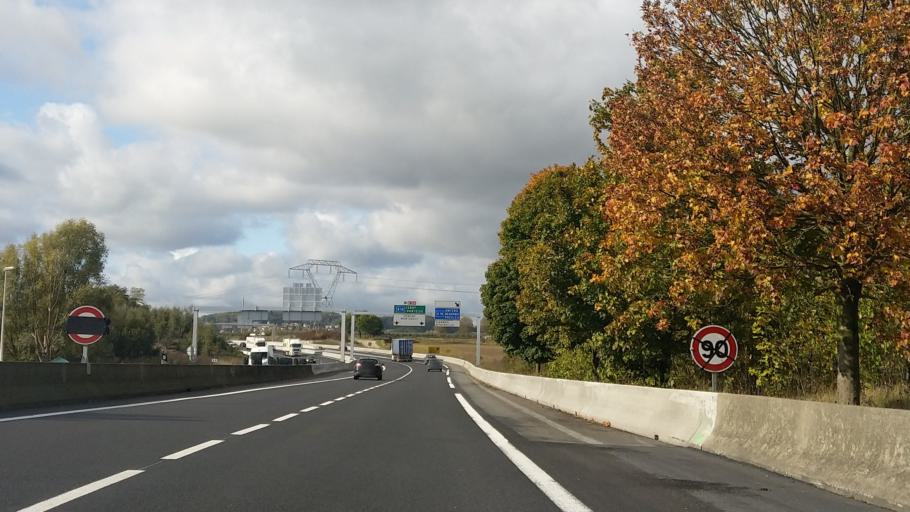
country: FR
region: Ile-de-France
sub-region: Departement du Val-d'Oise
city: Attainville
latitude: 49.0604
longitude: 2.3481
